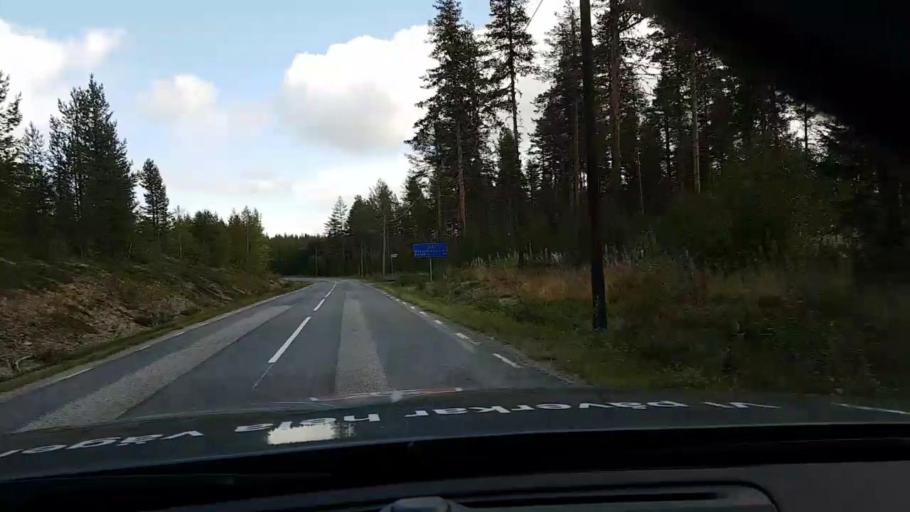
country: SE
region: Vaesterbotten
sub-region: Asele Kommun
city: Asele
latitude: 63.7945
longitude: 17.5690
